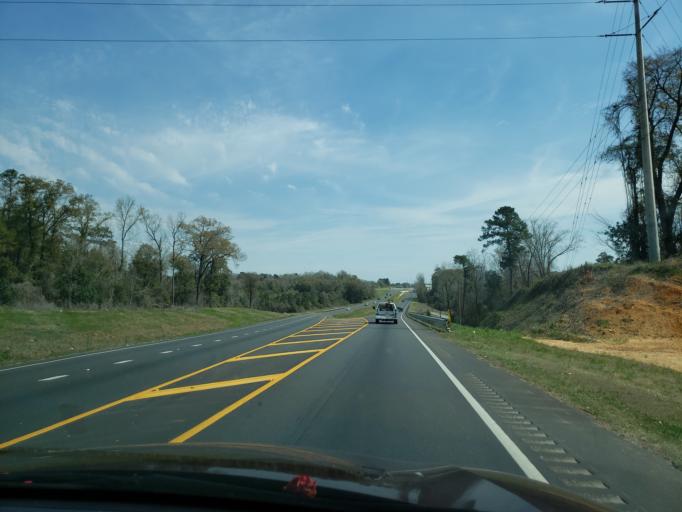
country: US
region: Alabama
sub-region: Autauga County
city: Prattville
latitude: 32.4379
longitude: -86.4356
